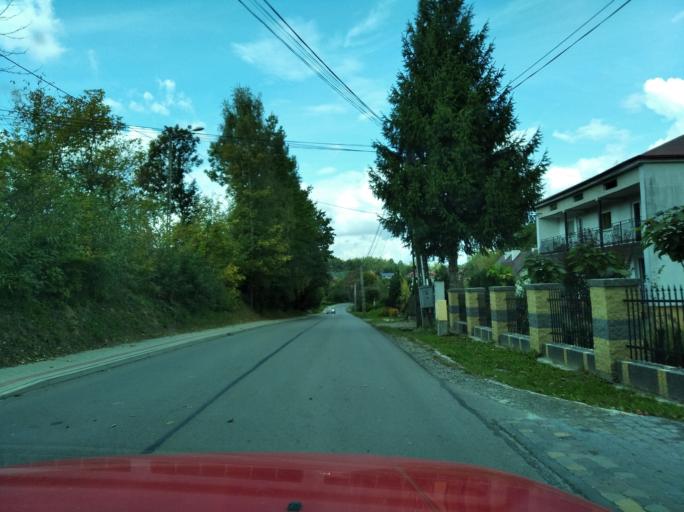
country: PL
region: Subcarpathian Voivodeship
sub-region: Powiat rzeszowski
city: Tyczyn
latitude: 49.9374
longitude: 22.0212
